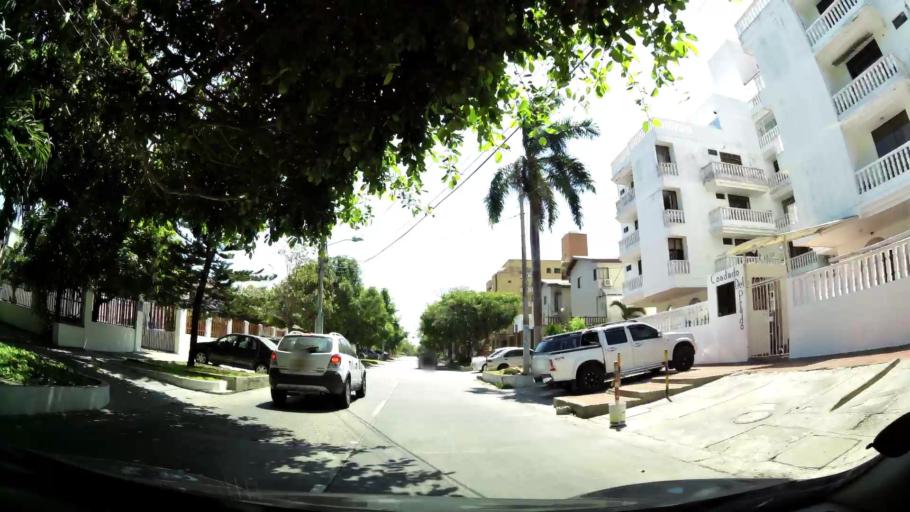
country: CO
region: Atlantico
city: Barranquilla
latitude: 11.0002
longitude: -74.7963
